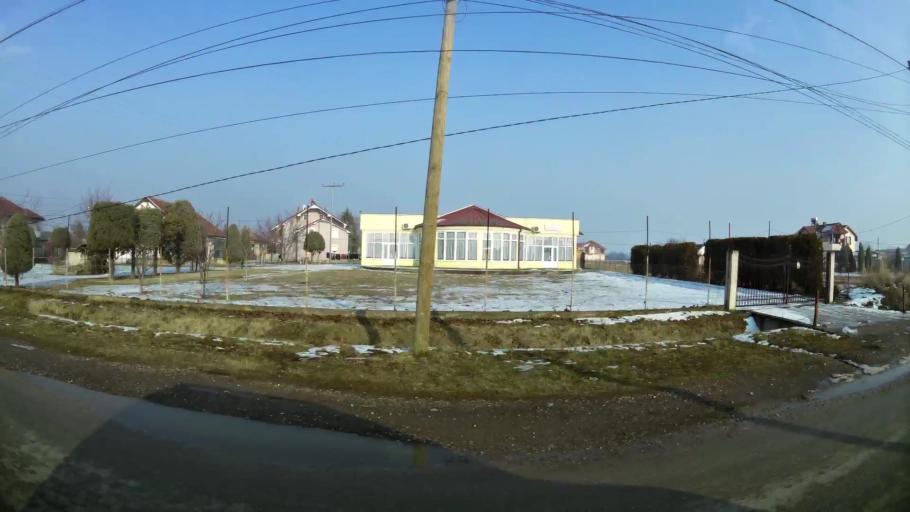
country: MK
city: Kadino
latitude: 41.9637
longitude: 21.5982
